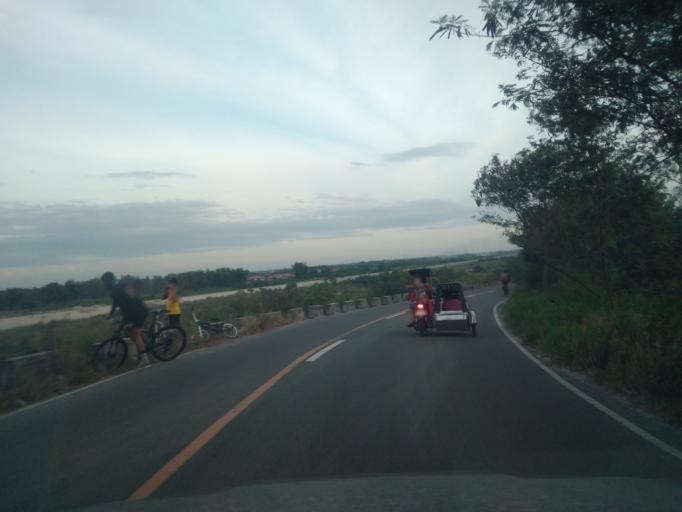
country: PH
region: Central Luzon
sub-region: Province of Pampanga
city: Santa Rita
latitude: 15.0201
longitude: 120.6199
